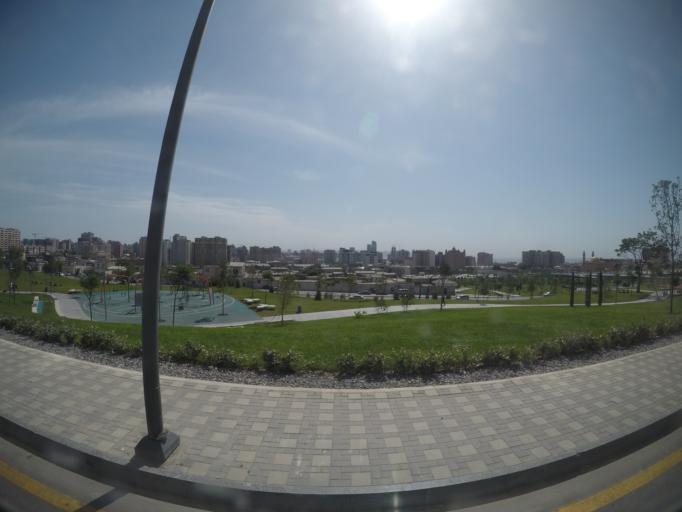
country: AZ
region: Baki
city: Badamdar
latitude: 40.3755
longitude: 49.8242
